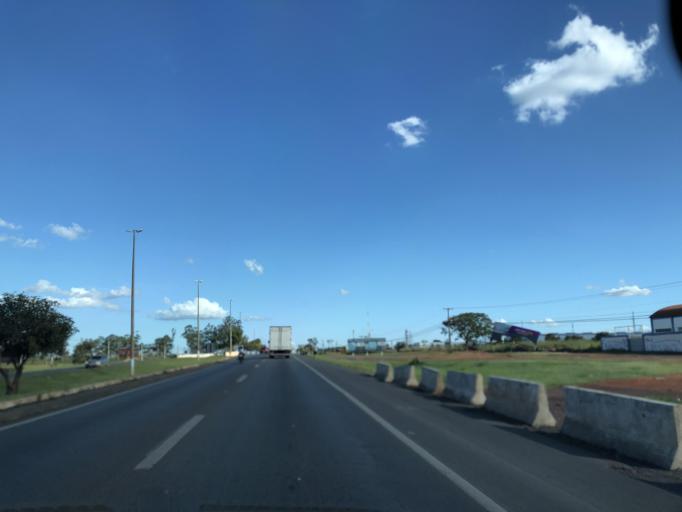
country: BR
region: Federal District
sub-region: Brasilia
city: Brasilia
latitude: -16.0128
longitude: -47.9822
